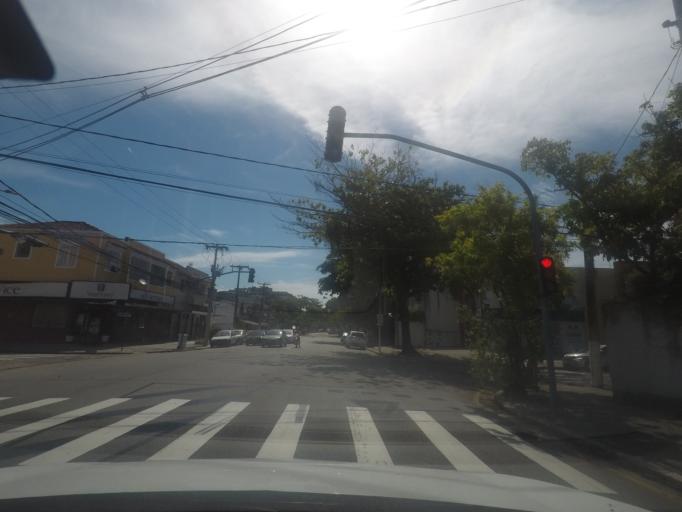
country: BR
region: Rio de Janeiro
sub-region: Niteroi
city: Niteroi
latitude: -22.9200
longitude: -43.0895
